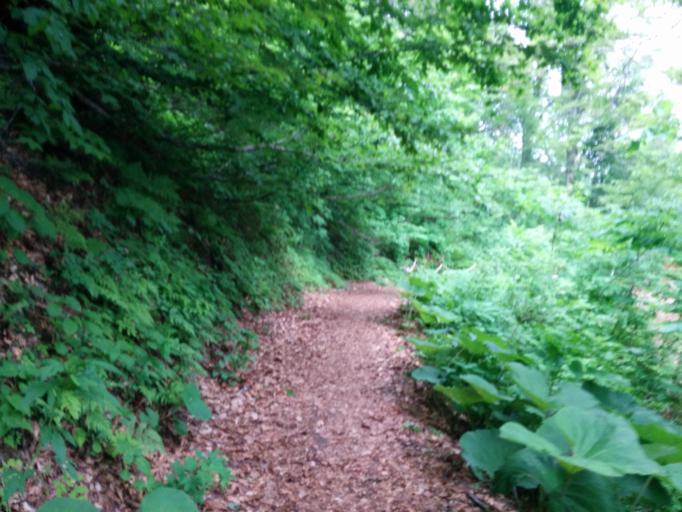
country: JP
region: Aomori
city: Hirosaki
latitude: 40.5543
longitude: 140.1649
